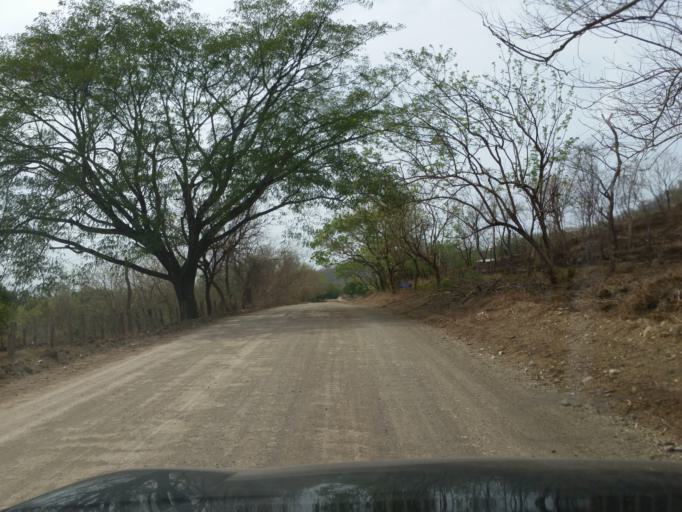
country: NI
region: Rivas
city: Tola
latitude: 11.4457
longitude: -86.0454
